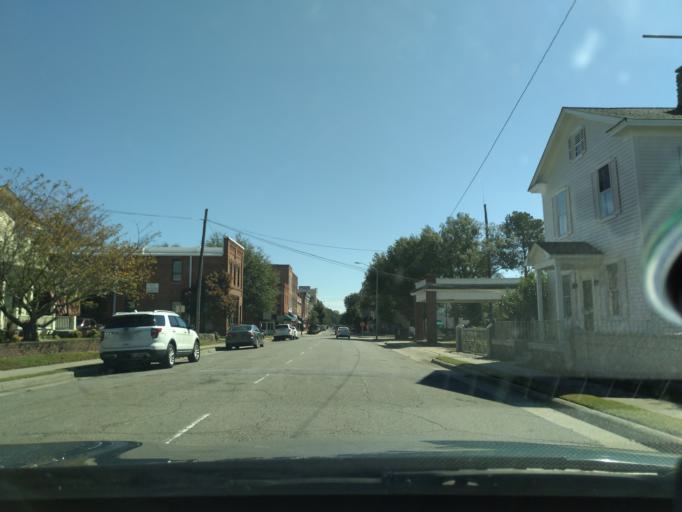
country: US
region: North Carolina
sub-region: Beaufort County
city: Washington
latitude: 35.5440
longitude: -77.0593
